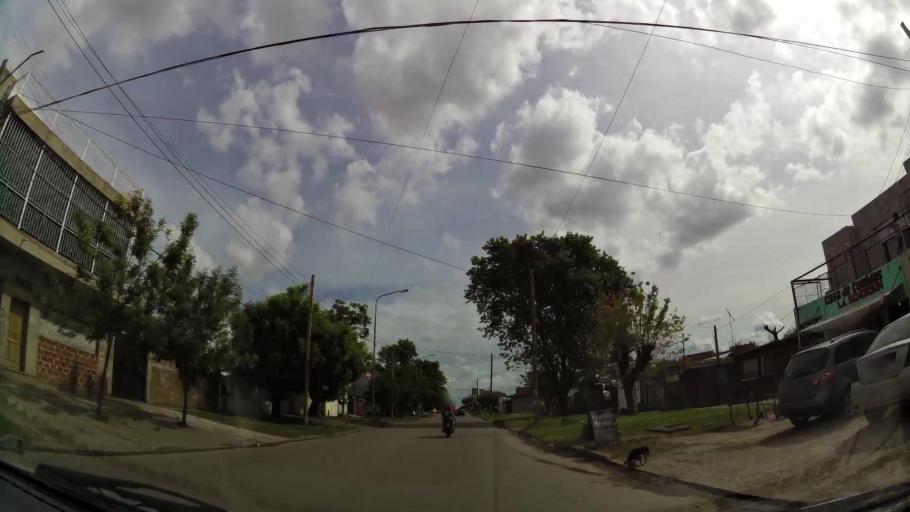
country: AR
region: Buenos Aires
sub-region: Partido de Quilmes
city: Quilmes
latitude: -34.7514
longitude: -58.2466
